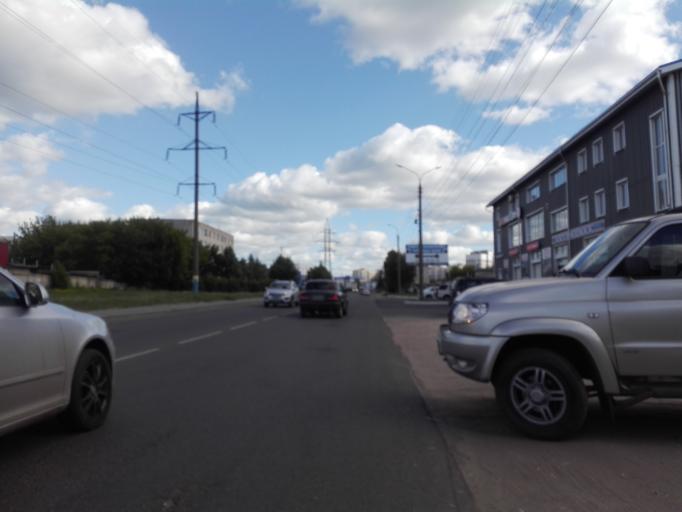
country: RU
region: Orjol
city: Orel
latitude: 52.9409
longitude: 36.0323
